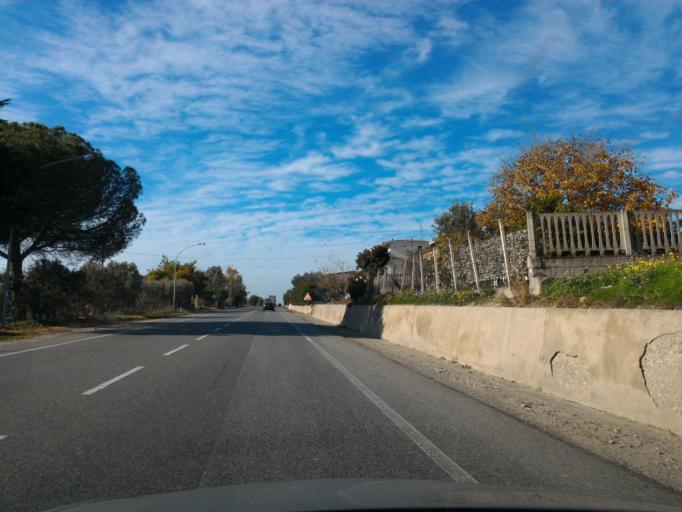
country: IT
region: Calabria
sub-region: Provincia di Catanzaro
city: Cropani Marina
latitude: 38.9275
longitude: 16.8259
